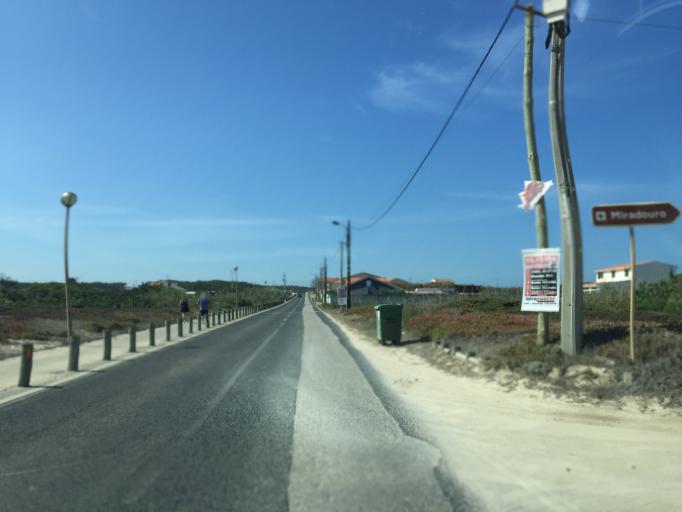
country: PT
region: Lisbon
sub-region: Torres Vedras
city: Silveira
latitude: 39.1642
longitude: -9.3598
